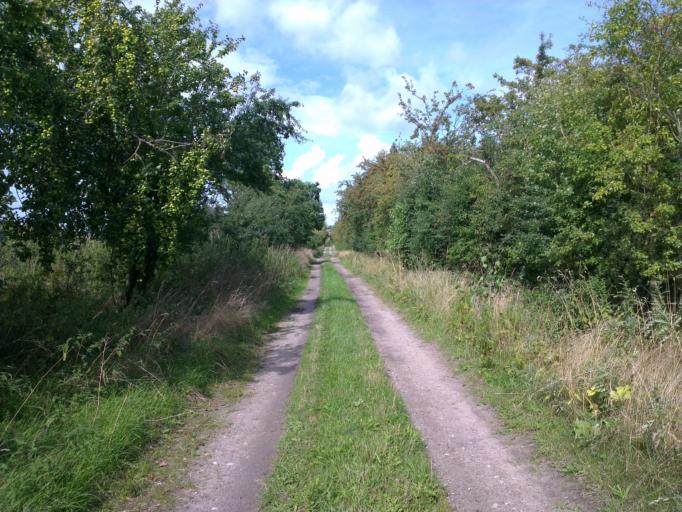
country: DK
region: Capital Region
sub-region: Frederikssund Kommune
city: Jaegerspris
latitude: 55.8520
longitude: 11.9737
